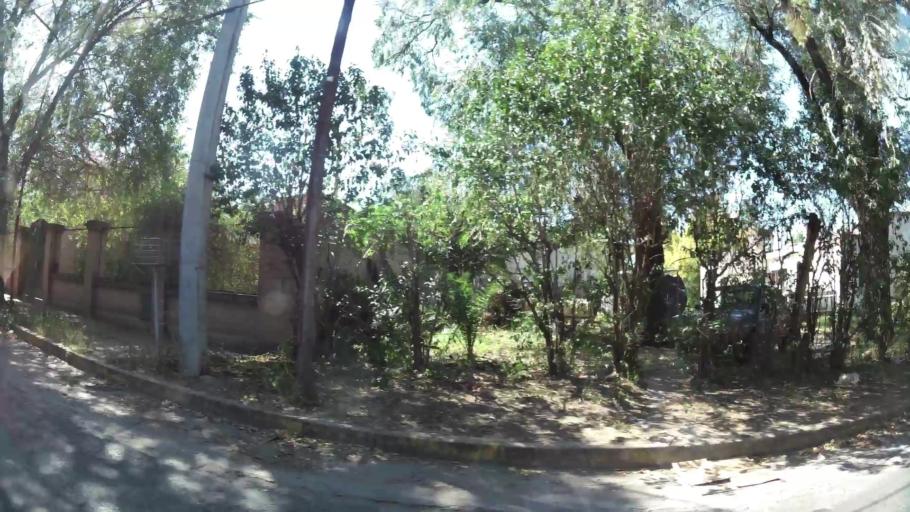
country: AR
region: Cordoba
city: Saldan
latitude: -31.2996
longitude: -64.3022
